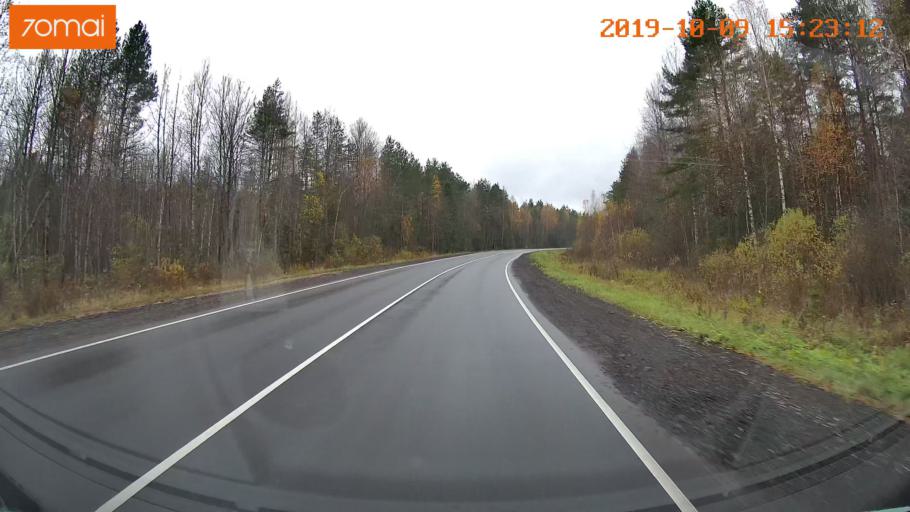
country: RU
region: Kostroma
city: Susanino
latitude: 58.0369
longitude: 41.4854
